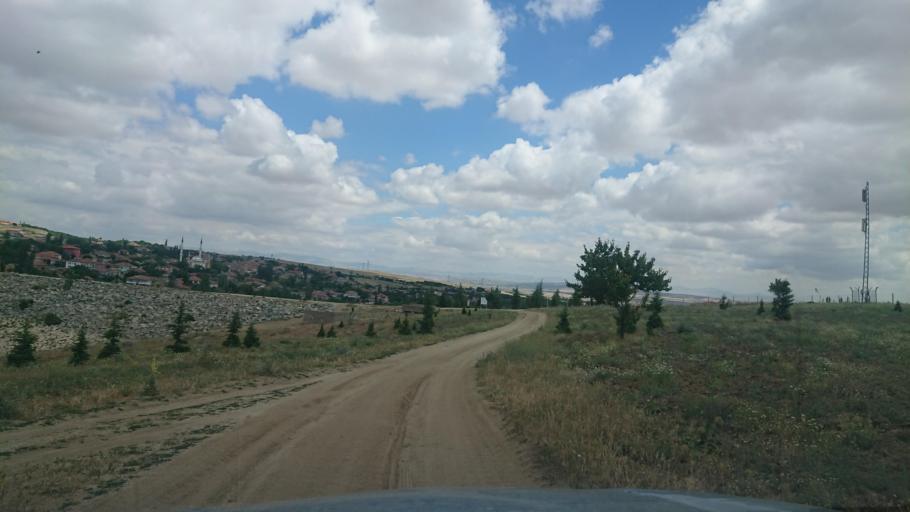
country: TR
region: Aksaray
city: Agacoren
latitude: 38.8638
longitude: 33.9510
